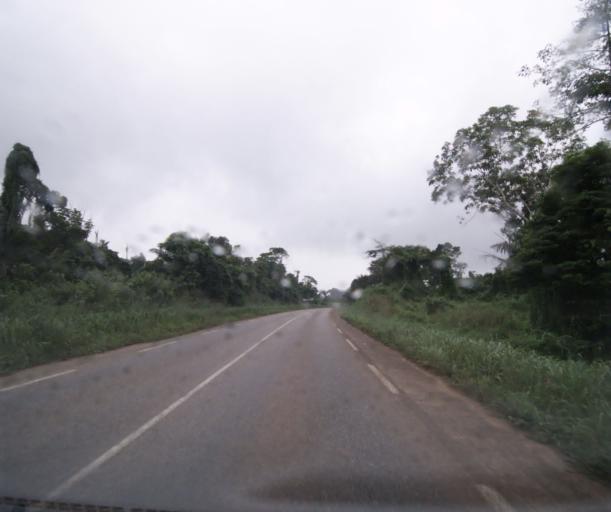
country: CM
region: Centre
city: Eseka
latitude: 3.8698
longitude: 10.6556
